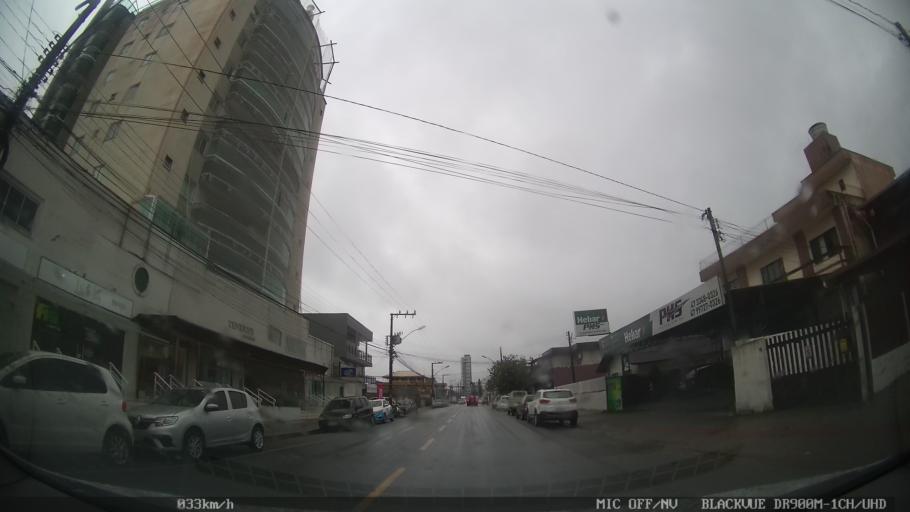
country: BR
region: Santa Catarina
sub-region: Itajai
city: Itajai
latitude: -26.9198
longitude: -48.6773
